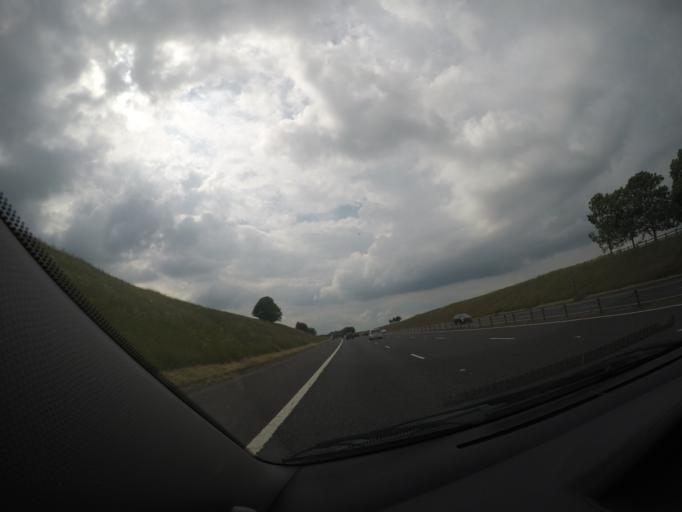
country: GB
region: Scotland
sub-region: Dumfries and Galloway
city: Annan
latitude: 55.0544
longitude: -3.2289
